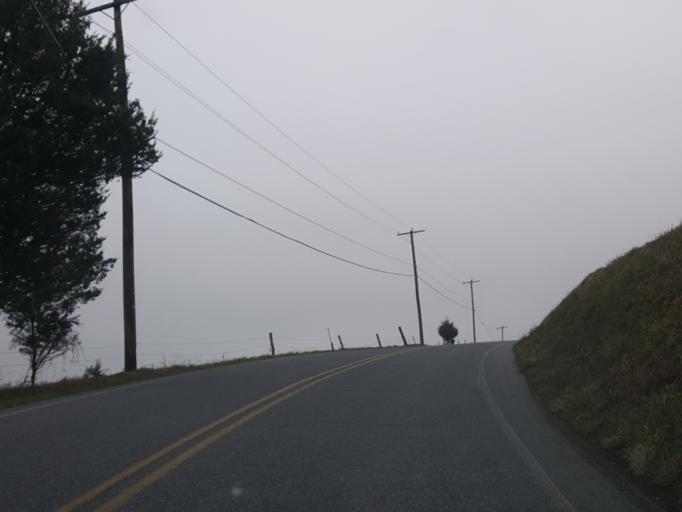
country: US
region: Pennsylvania
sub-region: Schuylkill County
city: Pine Grove
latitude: 40.5435
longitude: -76.4657
